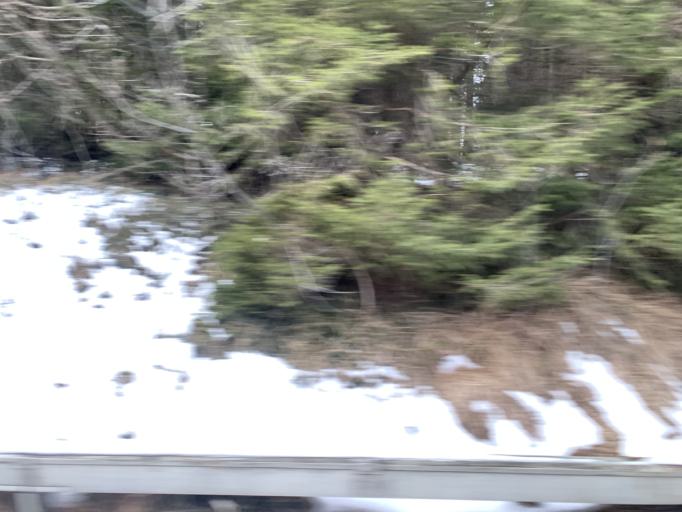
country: DE
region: Bavaria
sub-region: Upper Bavaria
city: Mittenwald
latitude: 47.4592
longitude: 11.2687
